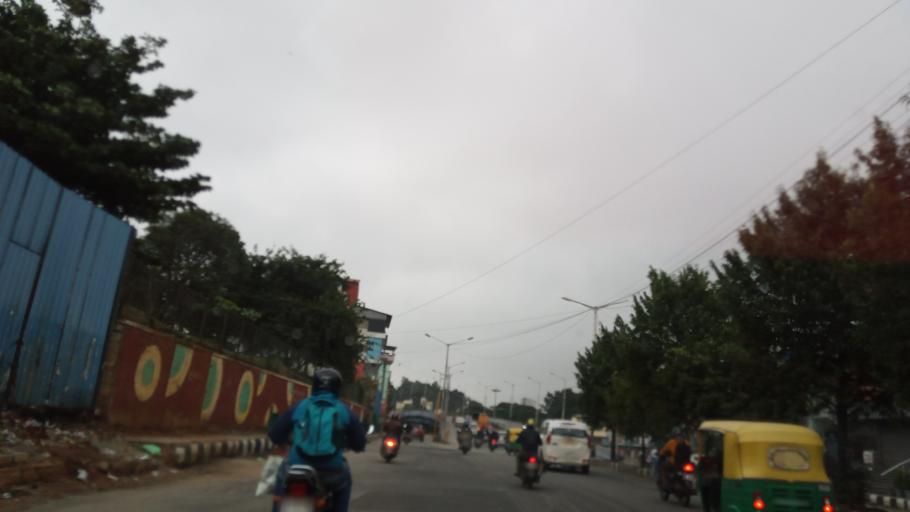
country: IN
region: Karnataka
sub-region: Bangalore Urban
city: Bangalore
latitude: 12.9224
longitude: 77.5581
